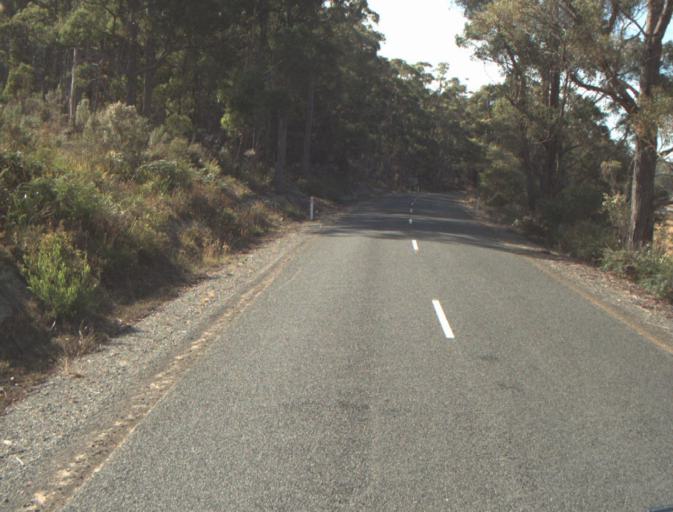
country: AU
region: Tasmania
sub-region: Dorset
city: Bridport
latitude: -41.1462
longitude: 147.2315
